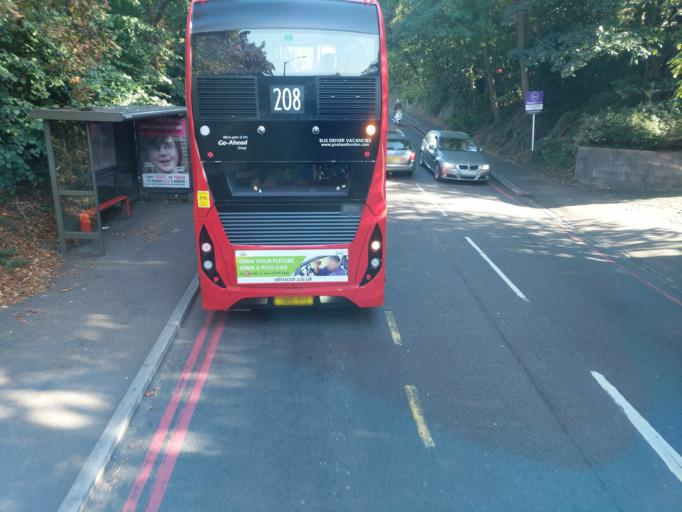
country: GB
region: England
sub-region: Greater London
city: Bromley
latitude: 51.4170
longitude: 0.0041
